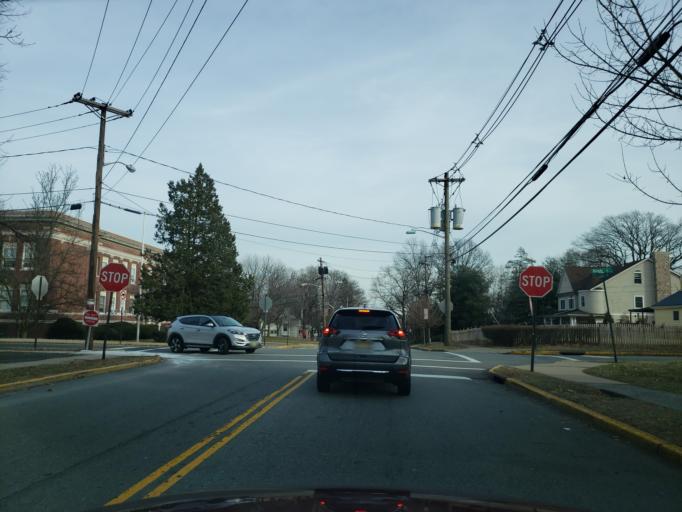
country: US
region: New Jersey
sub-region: Essex County
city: West Orange
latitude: 40.7992
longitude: -74.2229
